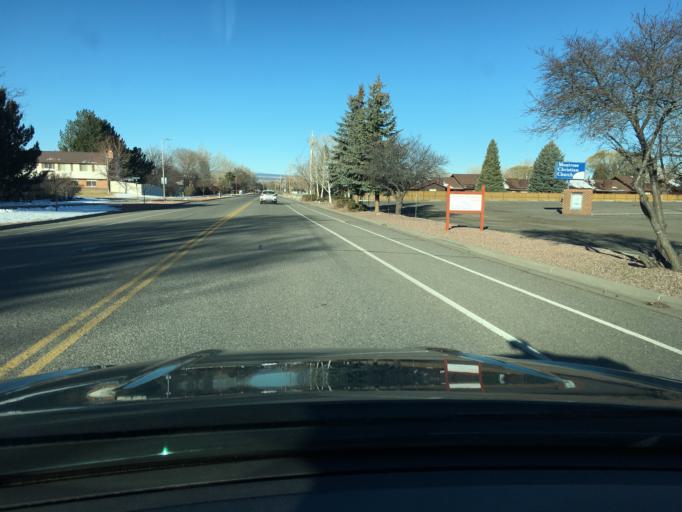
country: US
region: Colorado
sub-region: Montrose County
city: Montrose
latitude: 38.4746
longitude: -107.8495
